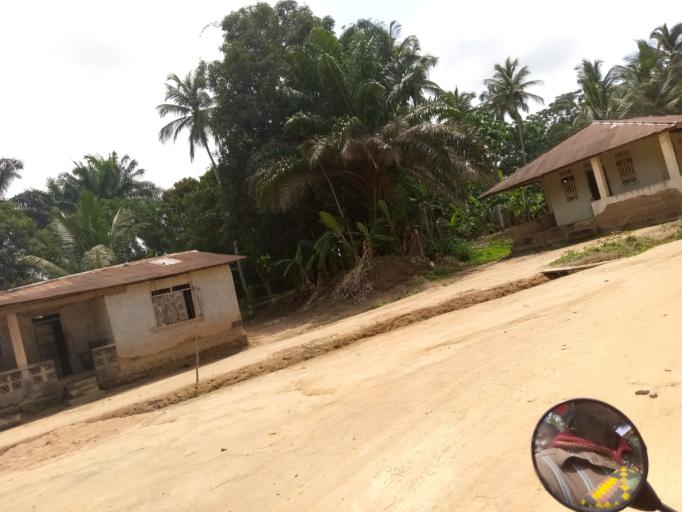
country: SL
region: Western Area
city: Waterloo
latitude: 8.3828
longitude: -12.9976
